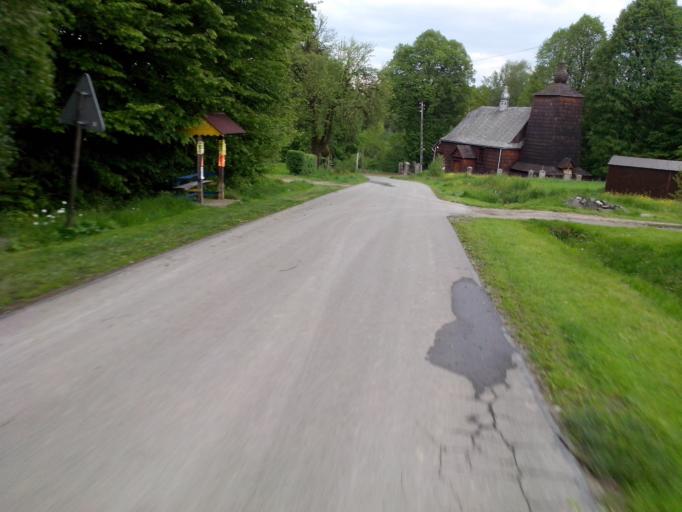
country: PL
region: Subcarpathian Voivodeship
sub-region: Powiat strzyzowski
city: Wysoka Strzyzowska
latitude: 49.7996
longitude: 21.7978
